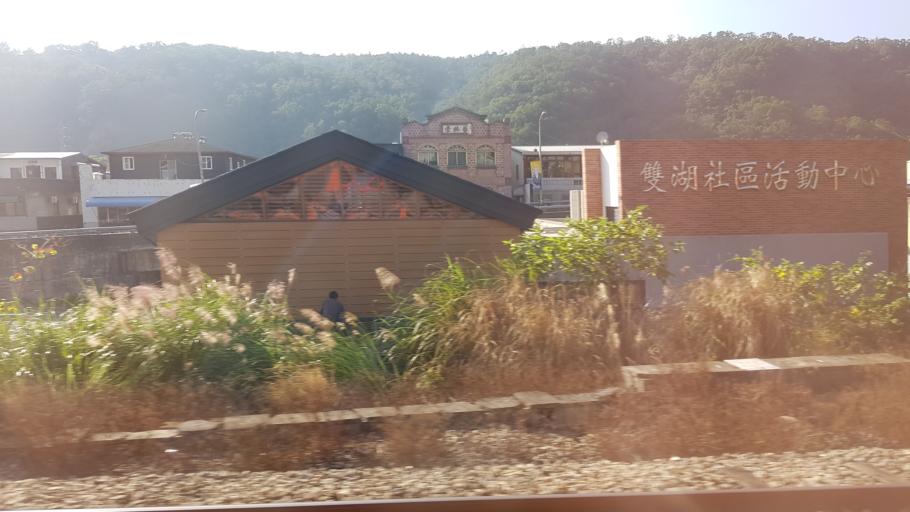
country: TW
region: Taiwan
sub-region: Miaoli
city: Miaoli
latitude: 24.4227
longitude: 120.7744
